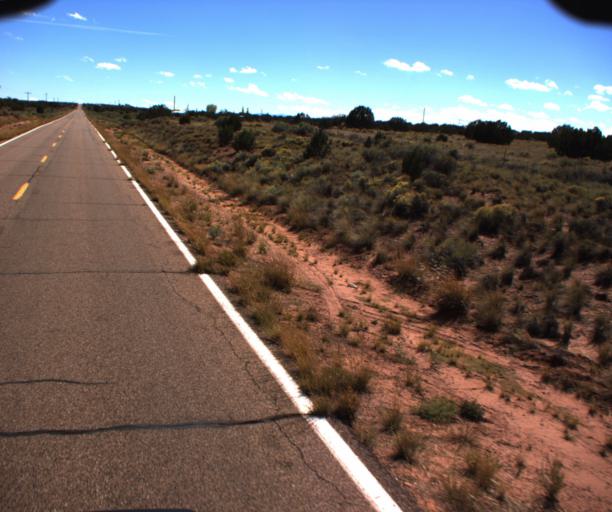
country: US
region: Arizona
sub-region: Apache County
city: Saint Johns
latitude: 34.6065
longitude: -109.6556
